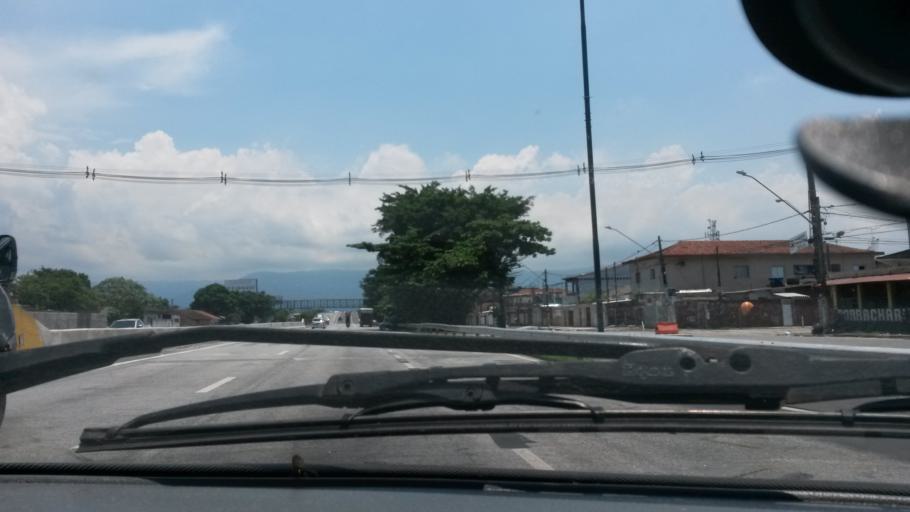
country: BR
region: Sao Paulo
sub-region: Sao Vicente
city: Sao Vicente
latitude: -23.9585
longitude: -46.4064
